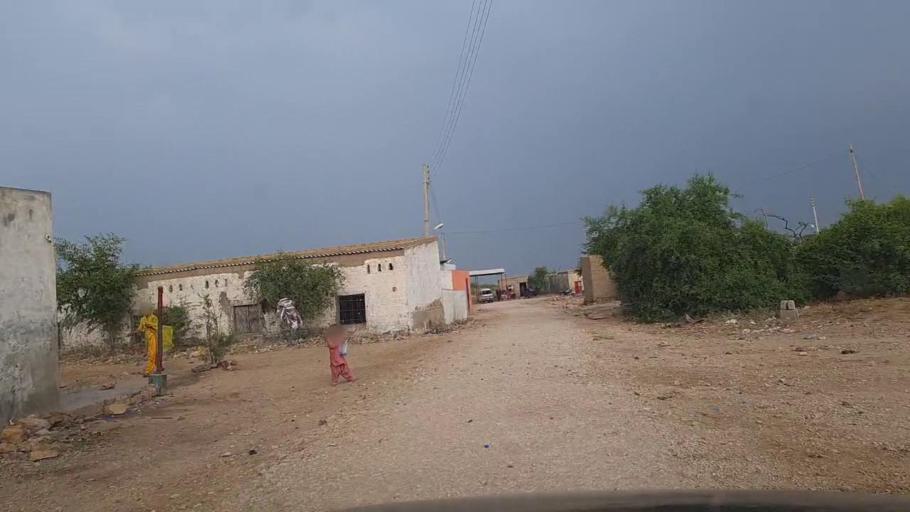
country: PK
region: Sindh
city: Gharo
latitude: 24.7825
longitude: 67.7492
